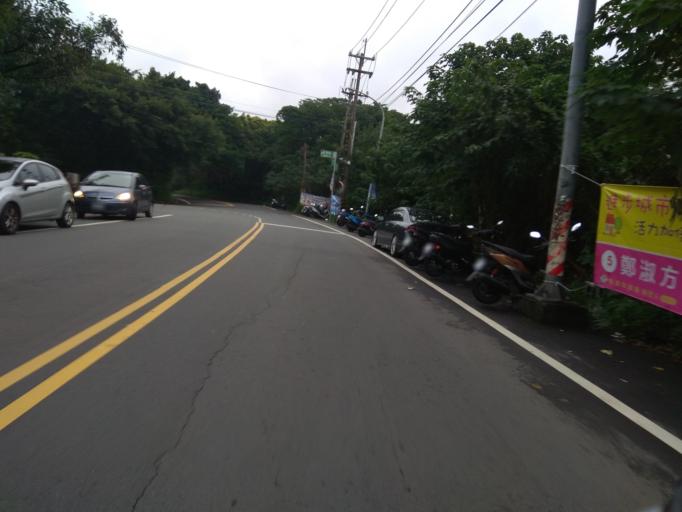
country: TW
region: Taiwan
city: Daxi
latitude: 24.9208
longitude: 121.1486
